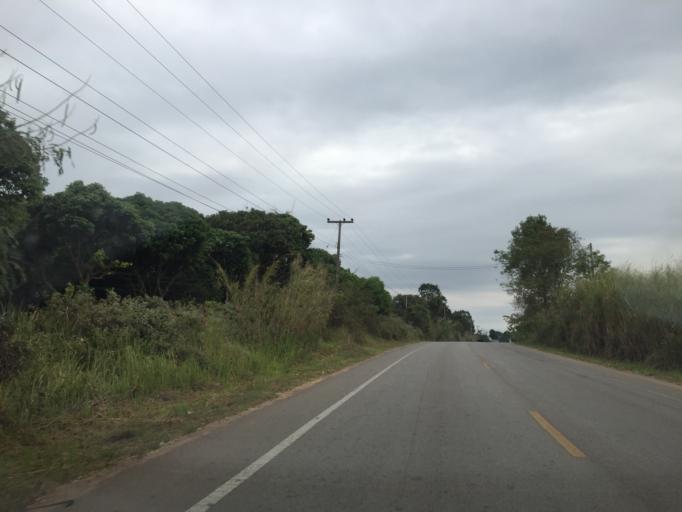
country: TH
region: Loei
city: Phu Ruea
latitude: 17.4464
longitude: 101.4942
